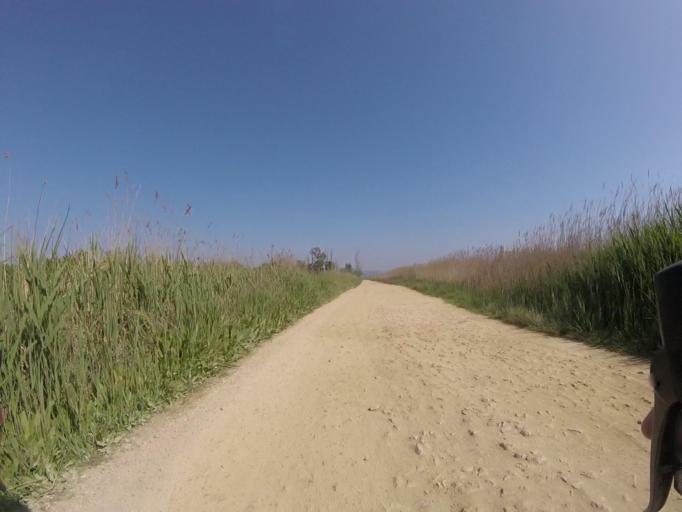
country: ES
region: Valencia
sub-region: Provincia de Castello
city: Torreblanca
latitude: 40.1616
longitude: 0.1721
